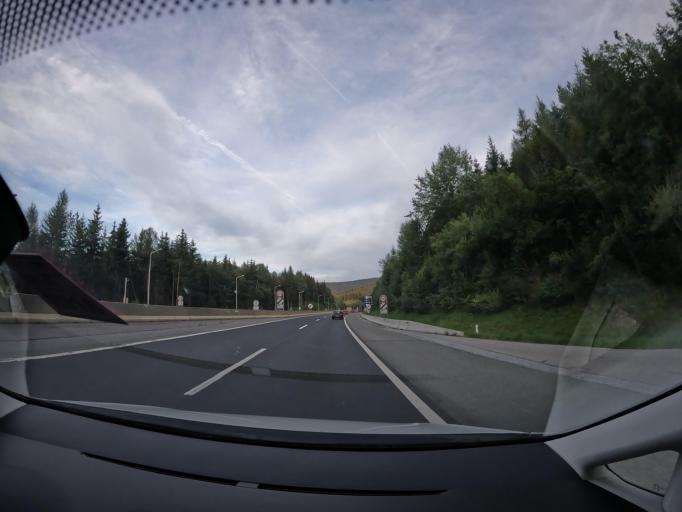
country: AT
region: Styria
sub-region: Politischer Bezirk Voitsberg
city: Modriach
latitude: 46.9831
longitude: 15.0909
